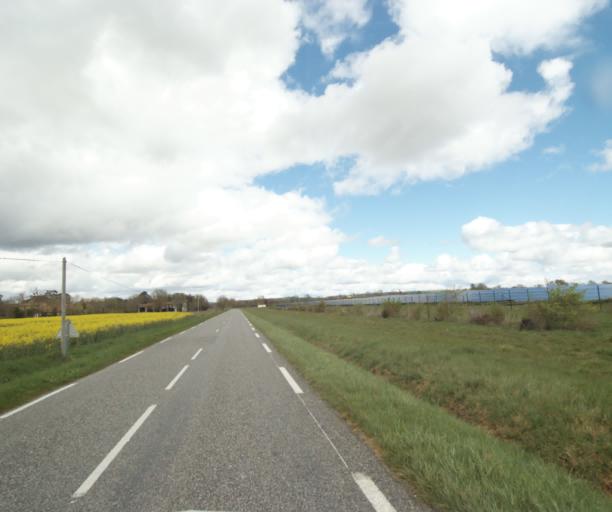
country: FR
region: Midi-Pyrenees
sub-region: Departement de l'Ariege
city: Mazeres
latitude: 43.2386
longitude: 1.6360
